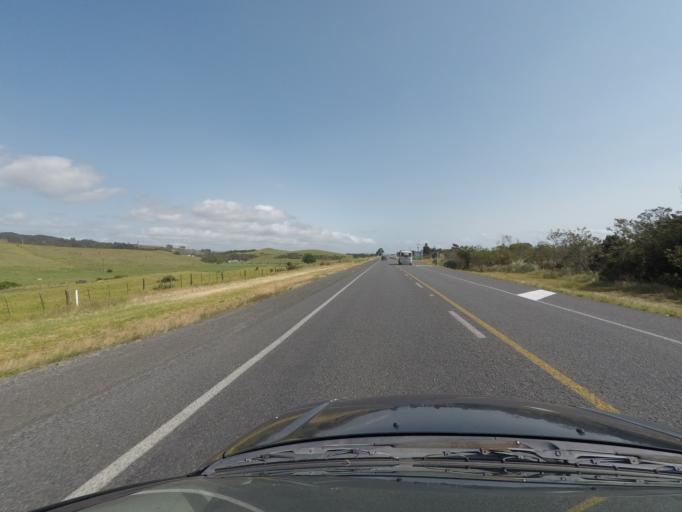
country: NZ
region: Northland
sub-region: Whangarei
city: Ruakaka
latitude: -35.9313
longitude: 174.4549
